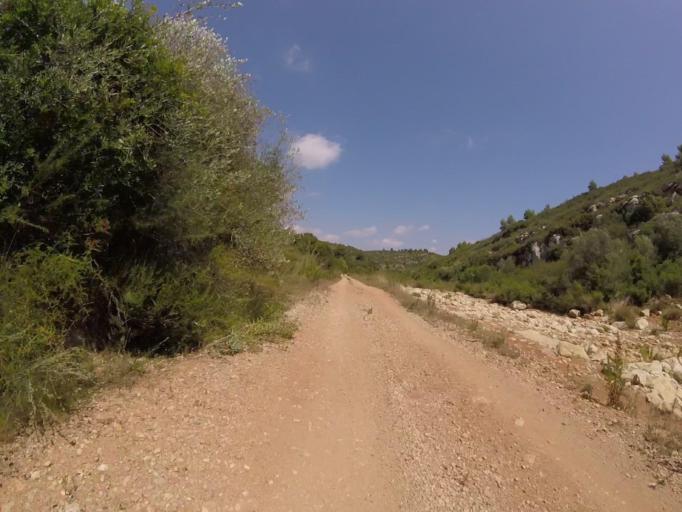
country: ES
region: Valencia
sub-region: Provincia de Castello
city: Torreblanca
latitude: 40.2164
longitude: 0.1477
